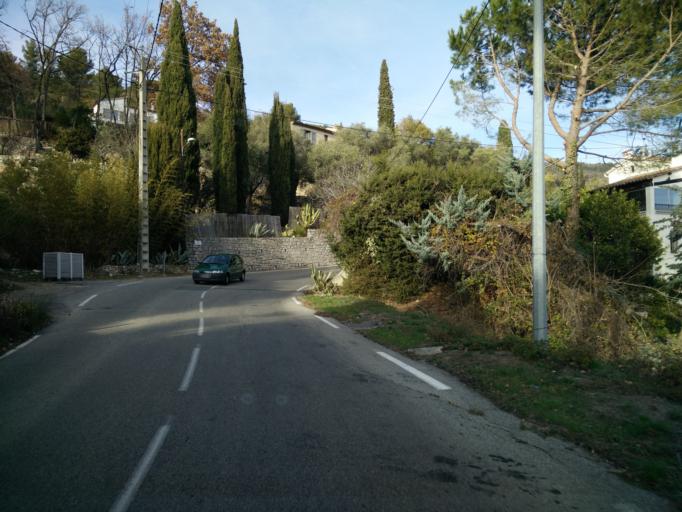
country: FR
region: Provence-Alpes-Cote d'Azur
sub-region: Departement des Alpes-Maritimes
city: Speracedes
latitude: 43.6438
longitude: 6.8541
